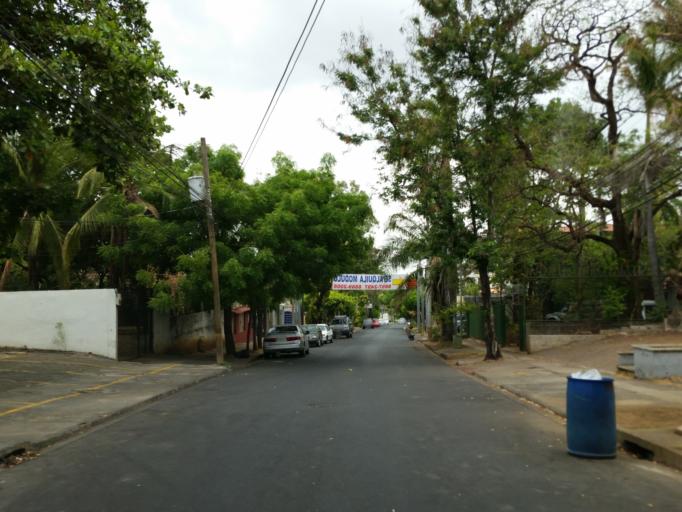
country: NI
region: Managua
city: Managua
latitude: 12.1190
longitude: -86.2630
